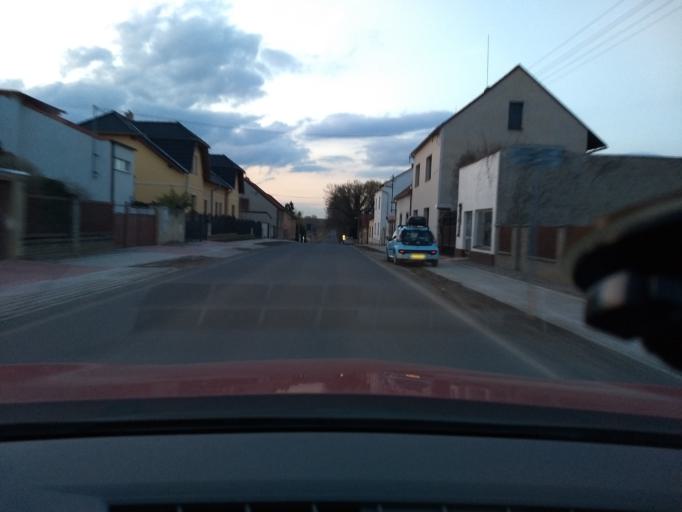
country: CZ
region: Central Bohemia
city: Jenec
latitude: 50.0618
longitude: 14.2256
